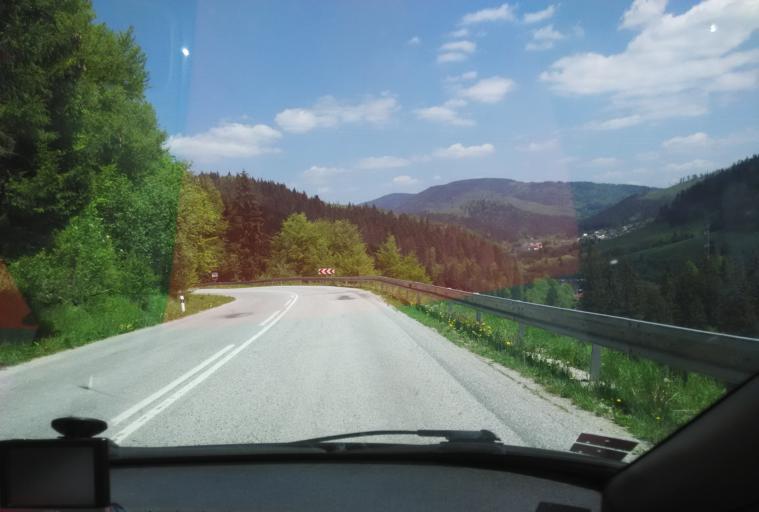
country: SK
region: Kosicky
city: Dobsina
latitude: 48.8532
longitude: 20.3807
